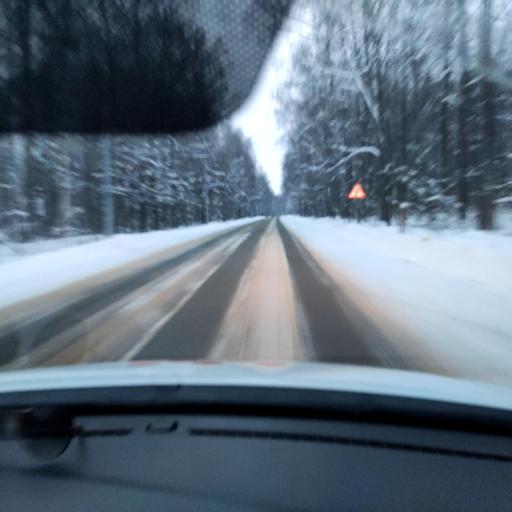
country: RU
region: Tatarstan
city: Vysokaya Gora
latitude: 55.9323
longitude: 49.1665
